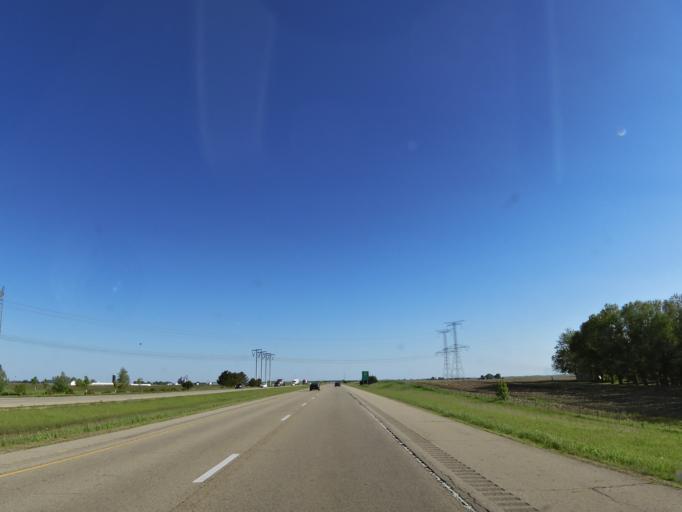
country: US
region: Illinois
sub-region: Woodford County
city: Minonk
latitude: 40.8675
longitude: -89.0367
